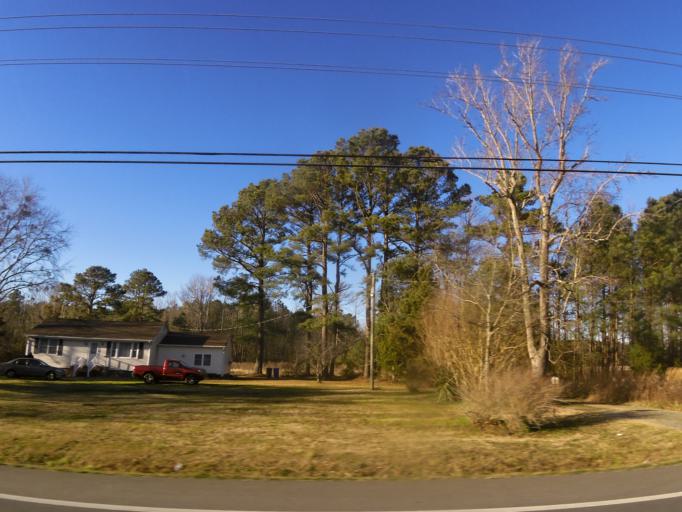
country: US
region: Virginia
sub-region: City of Suffolk
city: South Suffolk
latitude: 36.7056
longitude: -76.6867
